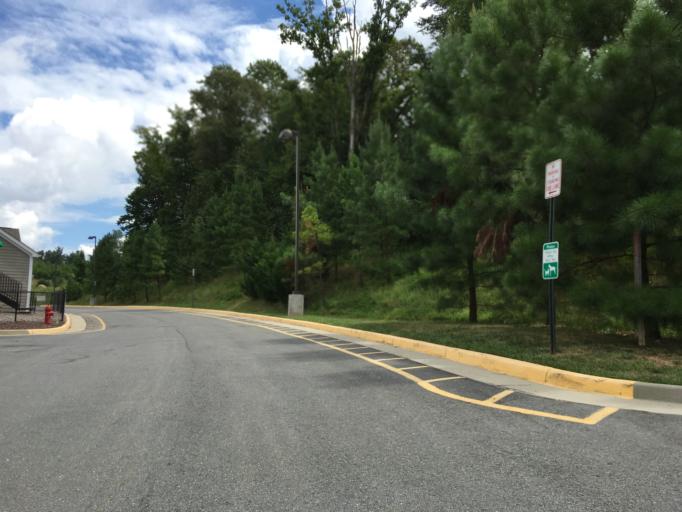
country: US
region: Virginia
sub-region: Greene County
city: Ruckersville
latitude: 38.1987
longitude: -78.3882
